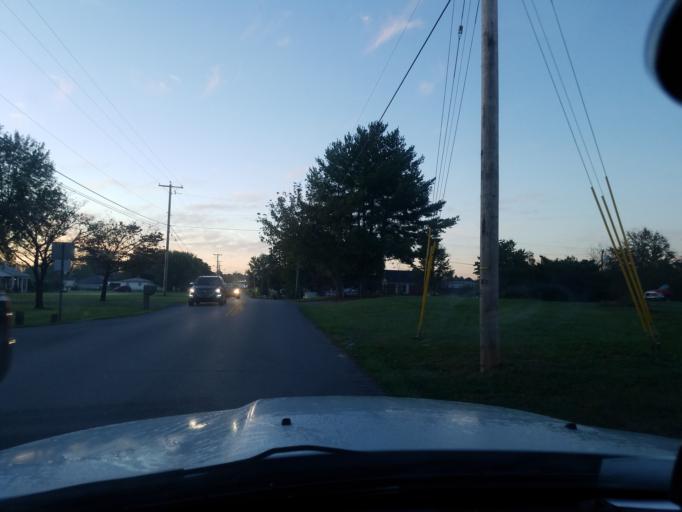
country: US
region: Kentucky
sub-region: Laurel County
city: London
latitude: 37.0959
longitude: -84.0843
